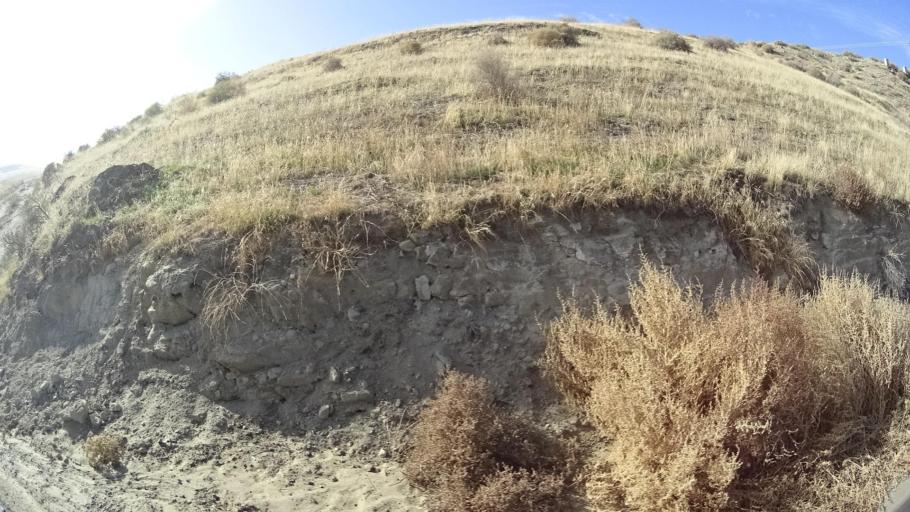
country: US
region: California
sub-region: Kern County
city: Oildale
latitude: 35.5126
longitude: -118.9009
